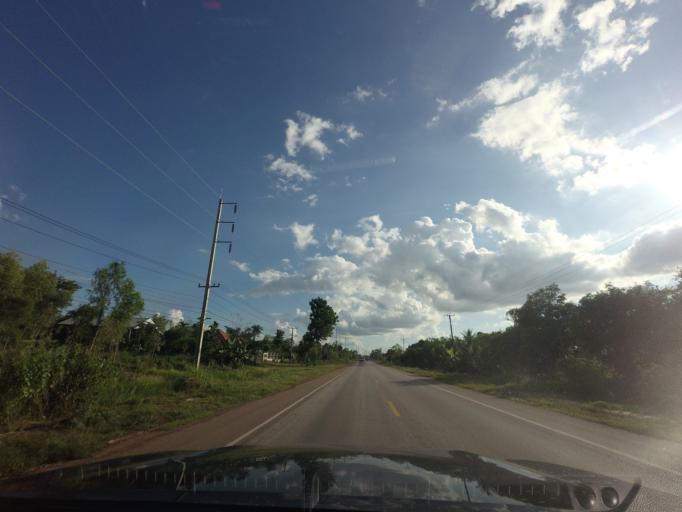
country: TH
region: Changwat Udon Thani
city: Thung Fon
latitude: 17.4944
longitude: 103.2003
